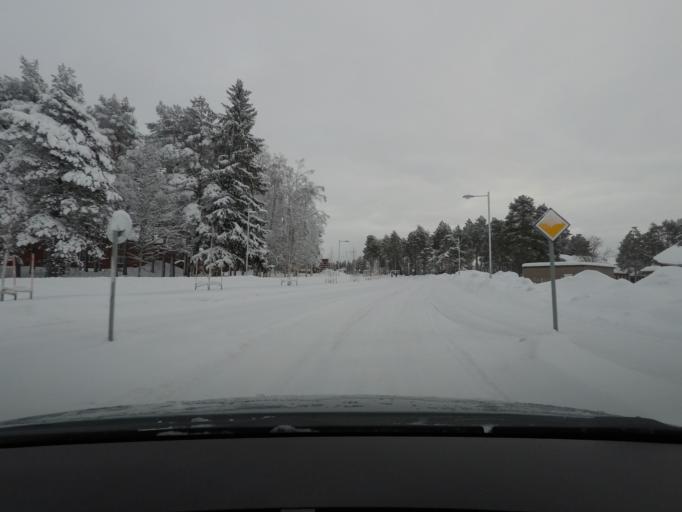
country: SE
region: Norrbotten
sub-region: Lulea Kommun
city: Lulea
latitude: 65.5932
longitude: 22.1884
